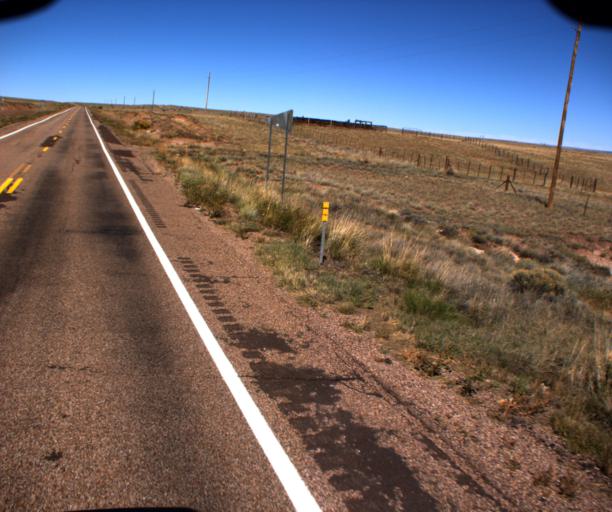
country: US
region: Arizona
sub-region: Apache County
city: Saint Johns
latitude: 34.5149
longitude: -109.4497
